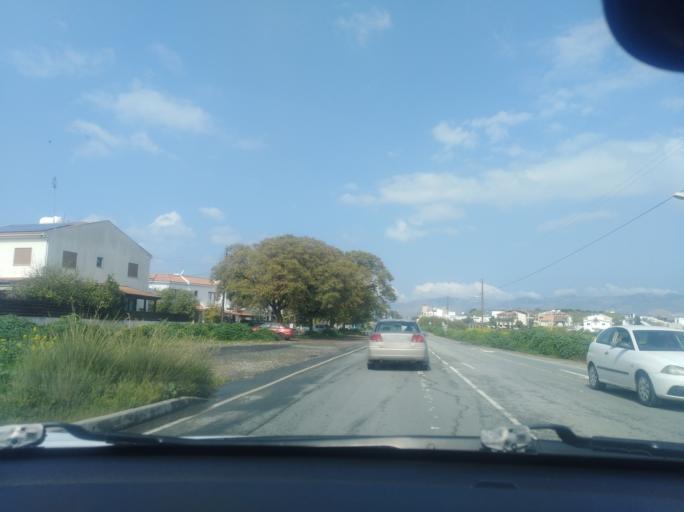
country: CY
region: Lefkosia
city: Nicosia
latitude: 35.1653
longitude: 33.3988
